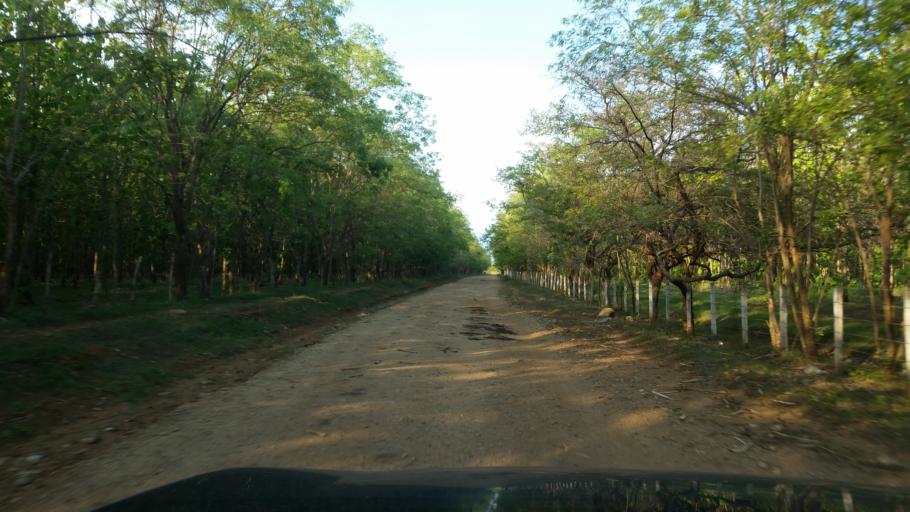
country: NI
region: Managua
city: Masachapa
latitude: 11.7742
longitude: -86.4878
